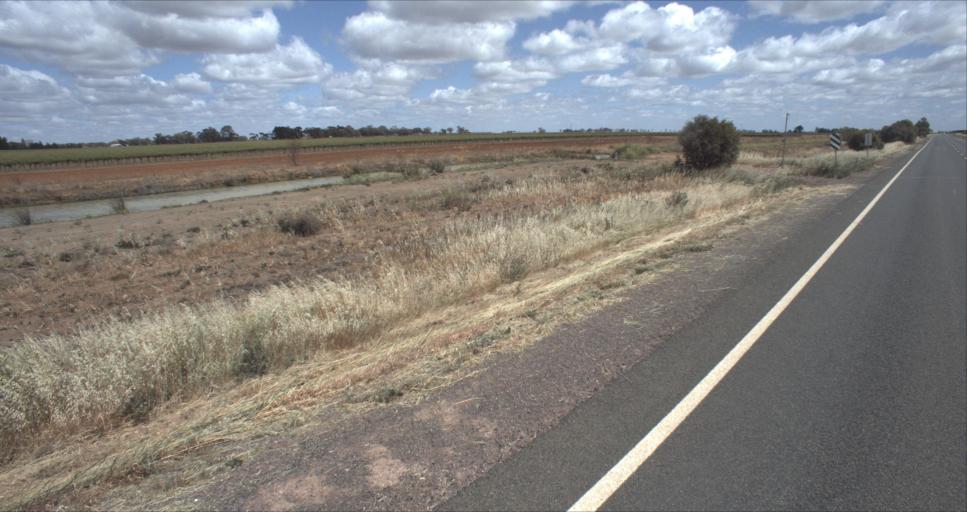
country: AU
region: New South Wales
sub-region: Murrumbidgee Shire
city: Darlington Point
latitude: -34.4815
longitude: 146.1549
